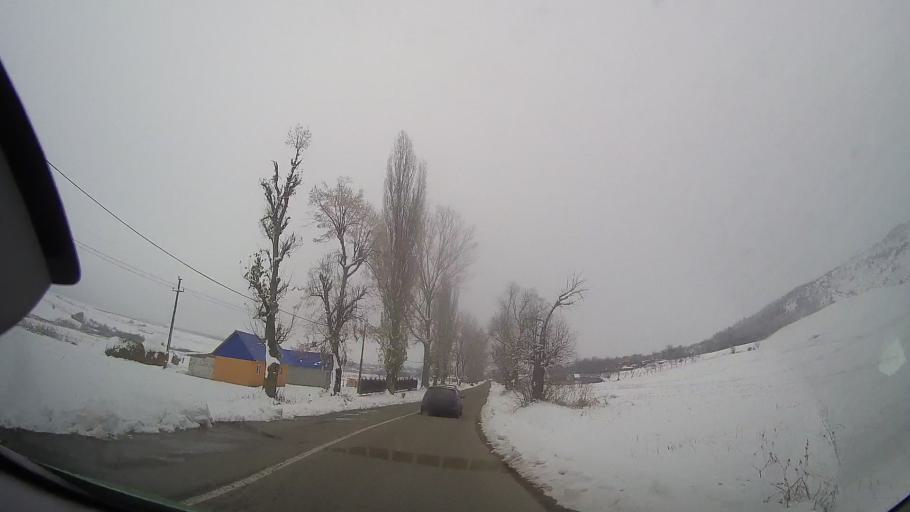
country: RO
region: Neamt
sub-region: Comuna Bozieni
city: Bozieni
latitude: 46.8319
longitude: 27.1754
